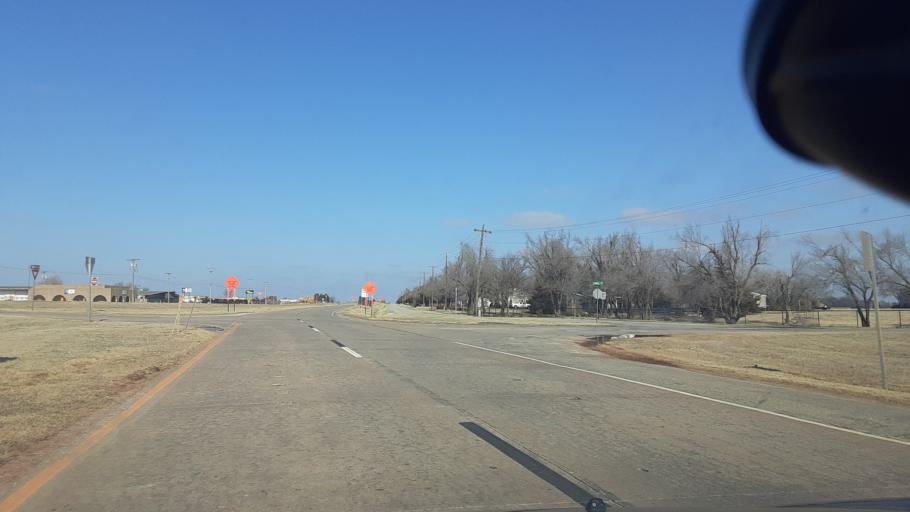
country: US
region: Oklahoma
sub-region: Garfield County
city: Enid
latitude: 36.4485
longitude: -97.8727
